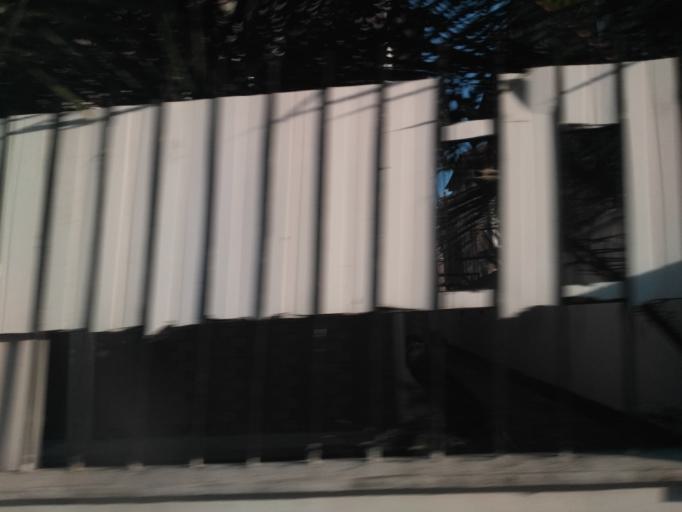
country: TZ
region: Dar es Salaam
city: Magomeni
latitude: -6.7651
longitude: 39.2625
